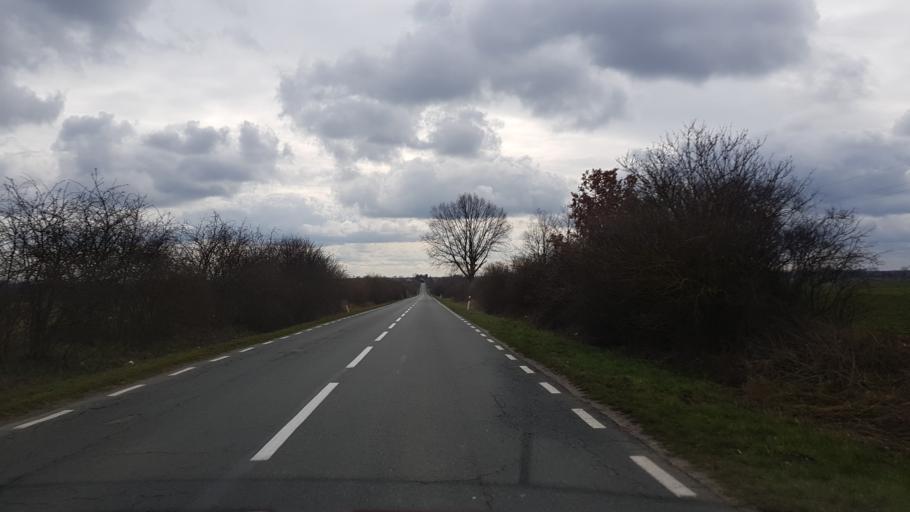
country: PL
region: West Pomeranian Voivodeship
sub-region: Powiat gryfinski
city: Banie
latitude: 53.1439
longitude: 14.6092
